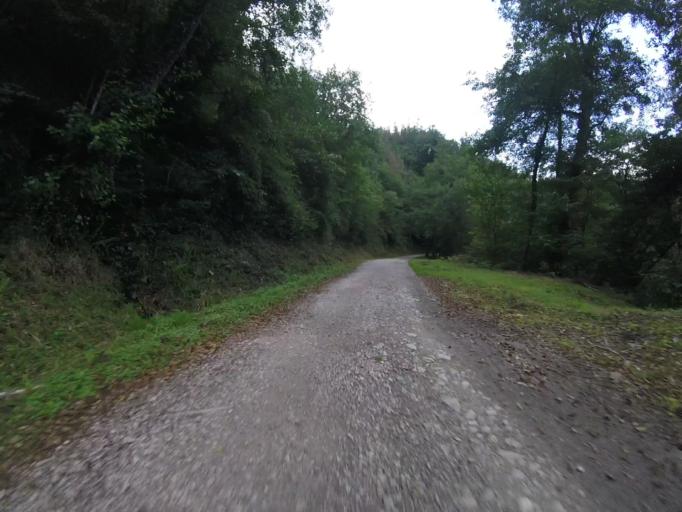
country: ES
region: Basque Country
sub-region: Provincia de Guipuzcoa
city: Berastegui
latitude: 43.1712
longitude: -1.9605
